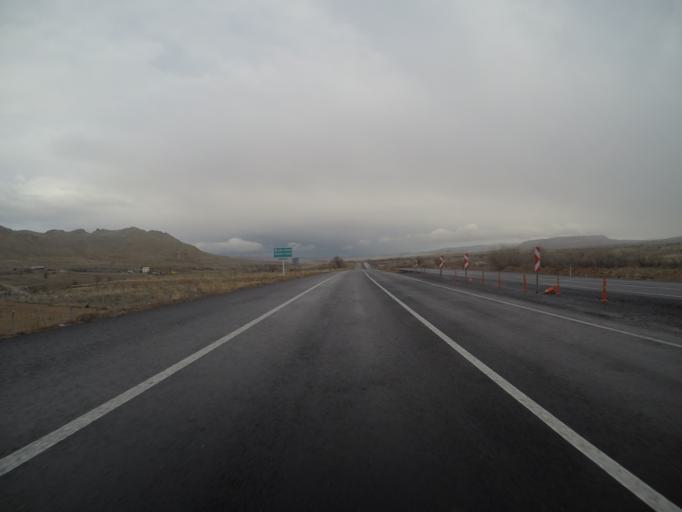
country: TR
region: Nevsehir
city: Goereme
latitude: 38.6818
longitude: 34.7939
